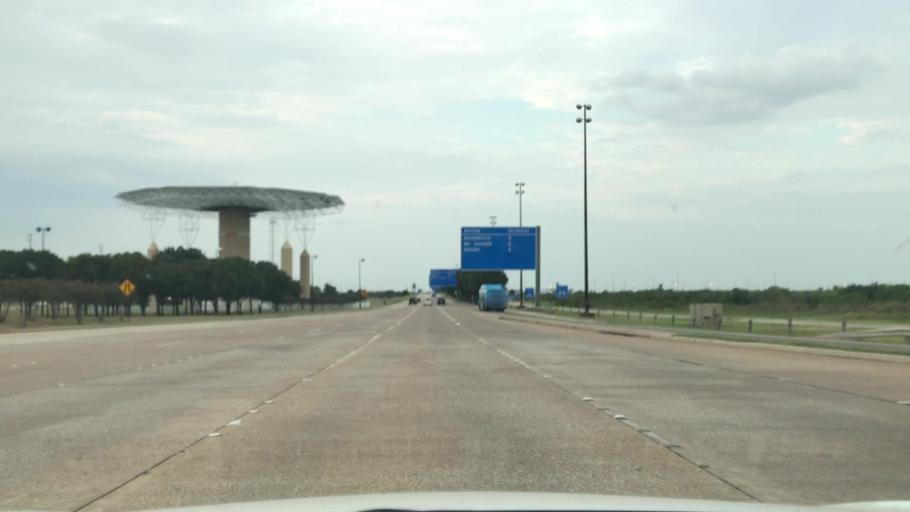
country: US
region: Texas
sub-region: Tarrant County
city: Euless
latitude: 32.8669
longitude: -97.0399
